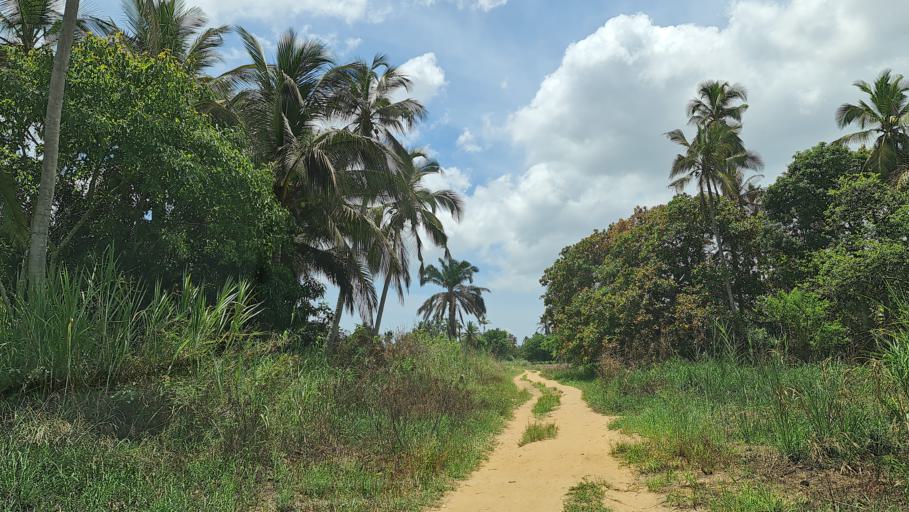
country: MZ
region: Zambezia
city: Quelimane
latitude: -17.5768
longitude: 37.3743
